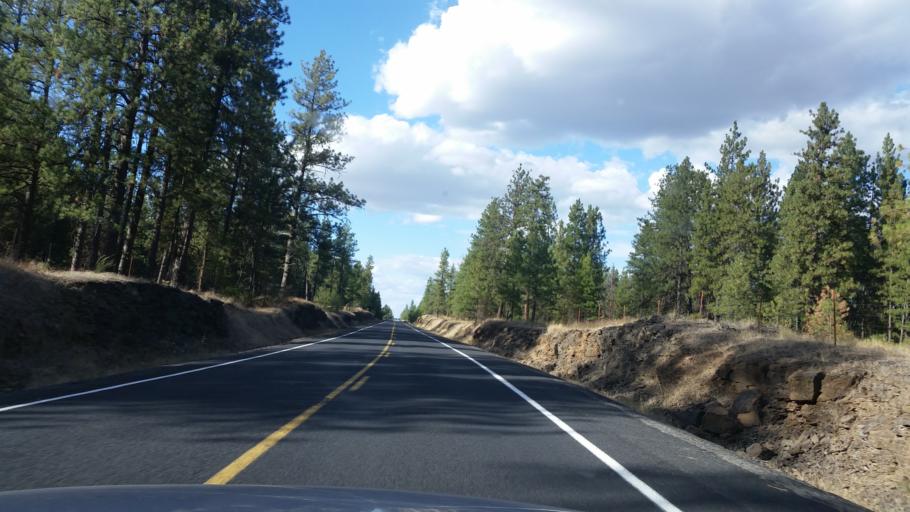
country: US
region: Washington
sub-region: Spokane County
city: Cheney
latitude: 47.4006
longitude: -117.5713
